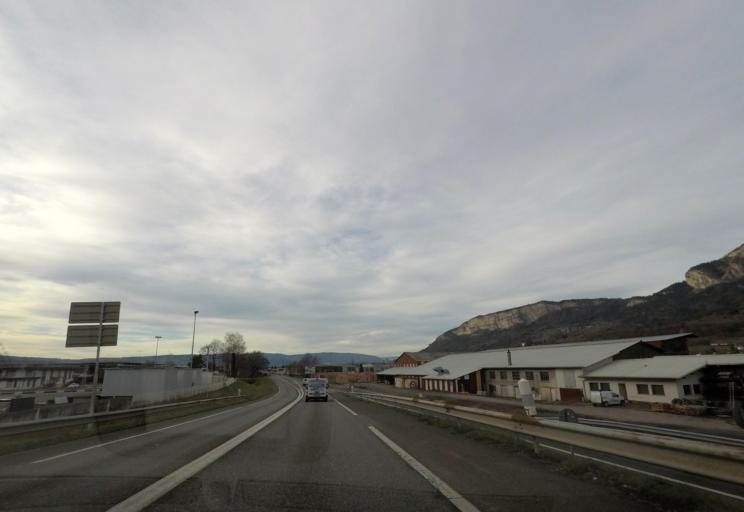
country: FR
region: Rhone-Alpes
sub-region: Departement de la Haute-Savoie
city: Ayse
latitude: 46.0706
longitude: 6.4303
